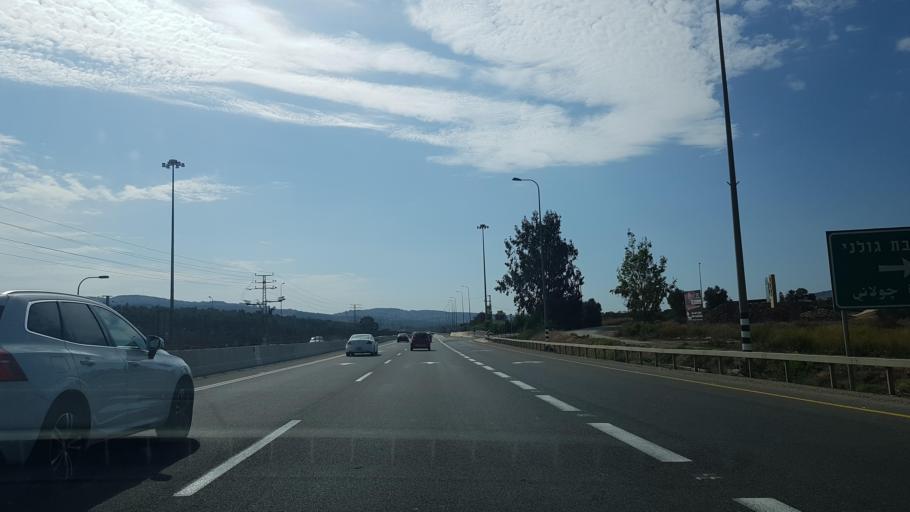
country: IL
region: Northern District
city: Bu`eina
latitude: 32.7720
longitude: 35.3933
